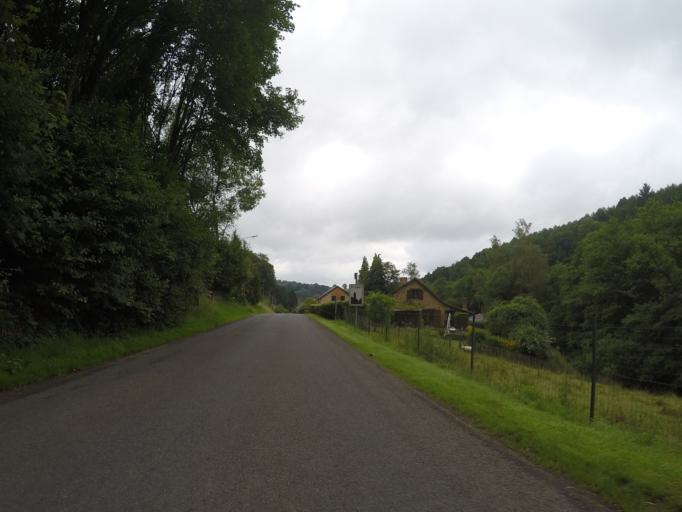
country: BE
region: Wallonia
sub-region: Province de Namur
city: Assesse
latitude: 50.3418
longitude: 4.9577
